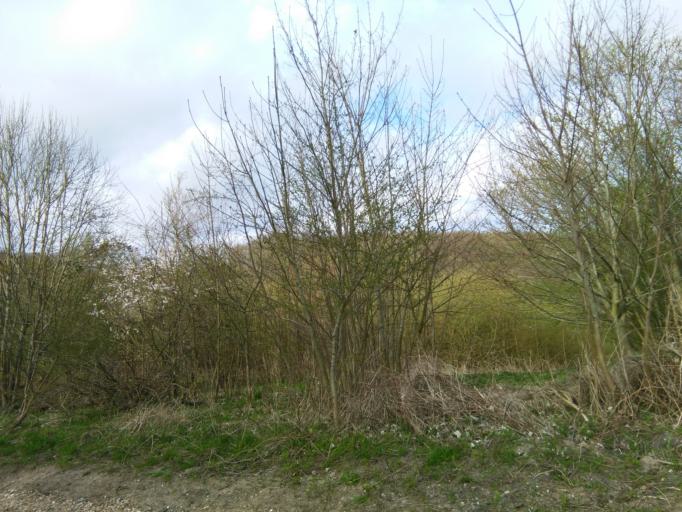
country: DK
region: Central Jutland
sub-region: Arhus Kommune
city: Beder
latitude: 56.0784
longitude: 10.1991
